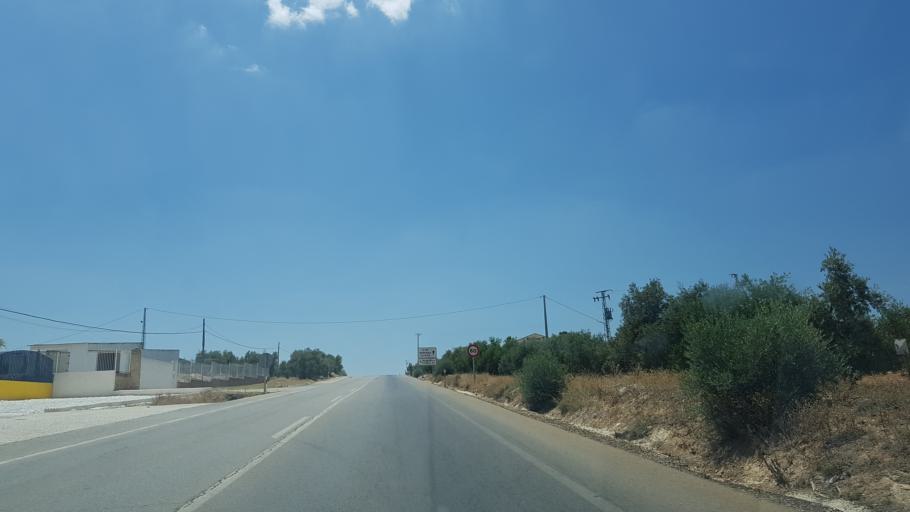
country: ES
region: Andalusia
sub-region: Provincia de Sevilla
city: Herrera
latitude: 37.3687
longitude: -4.8061
